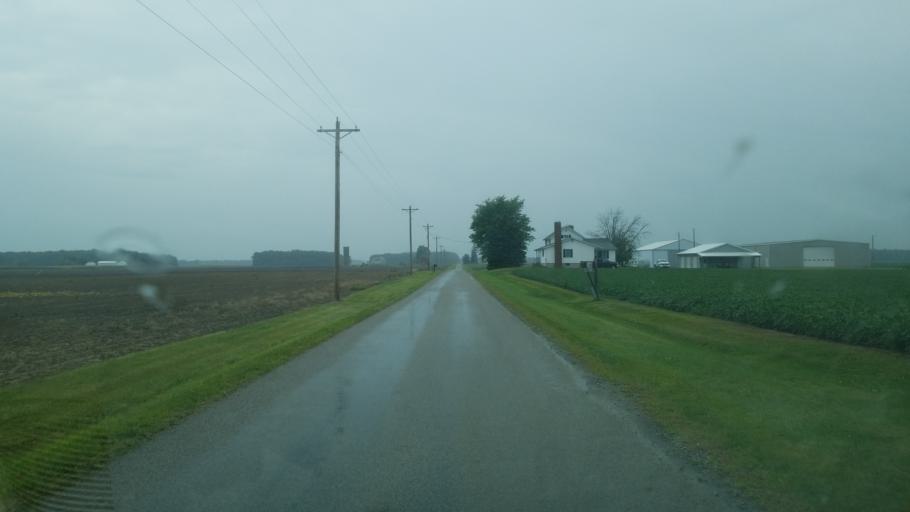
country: US
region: Ohio
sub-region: Huron County
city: Willard
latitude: 41.0105
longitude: -82.8022
